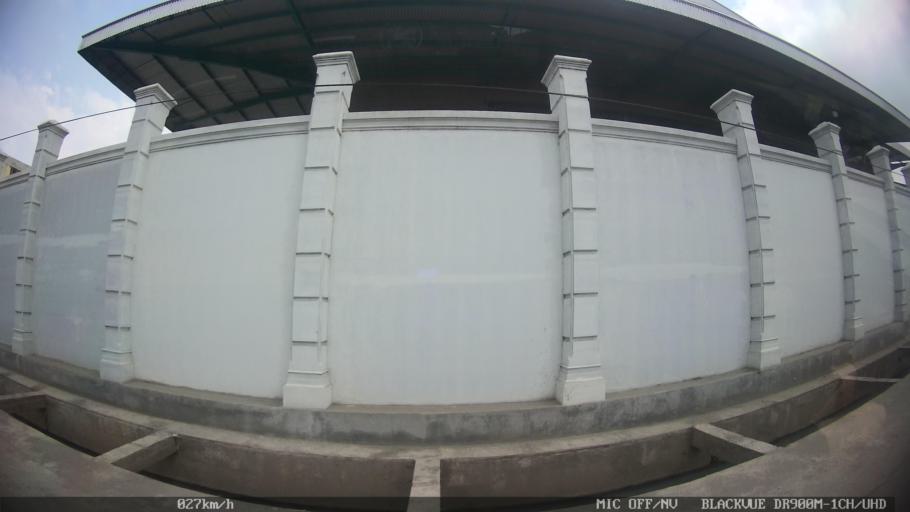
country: ID
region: North Sumatra
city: Medan
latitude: 3.6427
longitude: 98.6751
